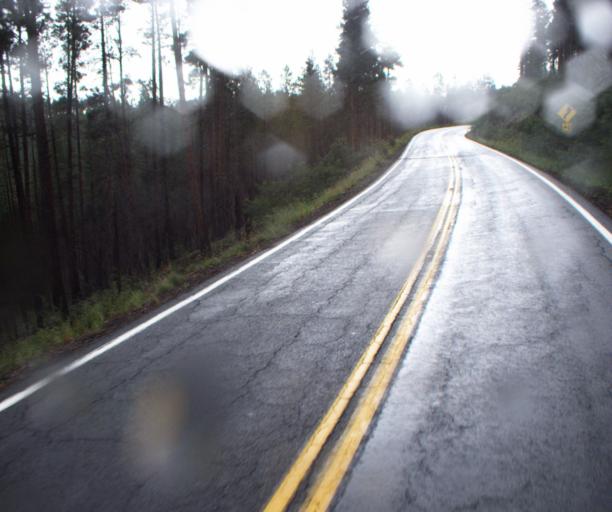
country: US
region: Arizona
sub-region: Apache County
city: Eagar
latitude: 33.7594
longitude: -109.2138
